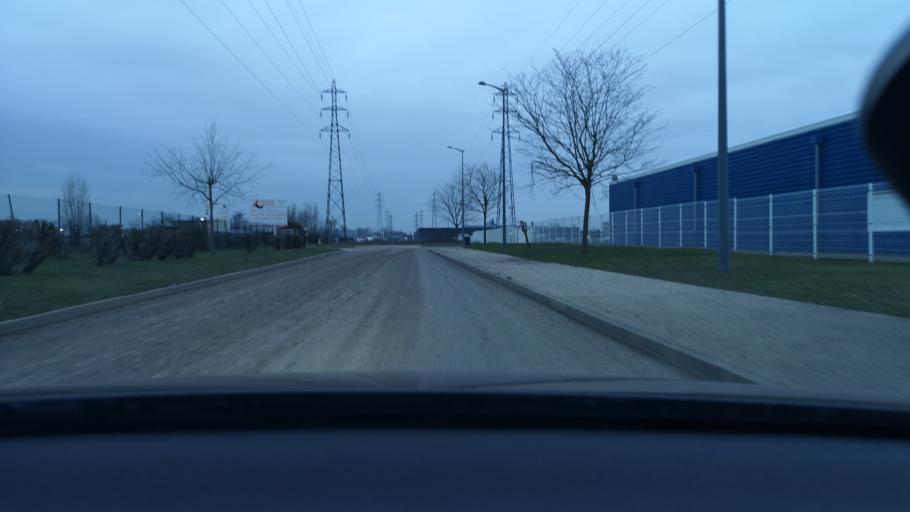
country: FR
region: Bourgogne
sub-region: Departement de Saone-et-Loire
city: Chalon-sur-Saone
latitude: 46.7651
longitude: 4.8667
